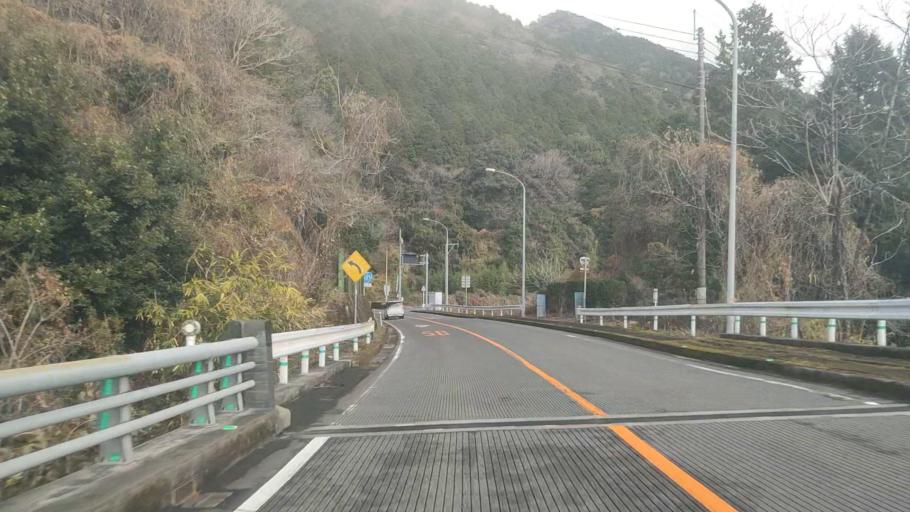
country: JP
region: Kumamoto
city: Hitoyoshi
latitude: 32.0721
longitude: 130.8010
